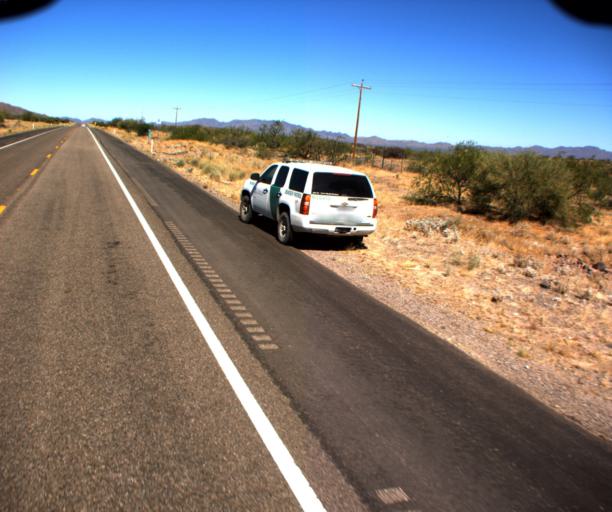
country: US
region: Arizona
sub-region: Pima County
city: Three Points
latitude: 32.0225
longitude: -111.5998
